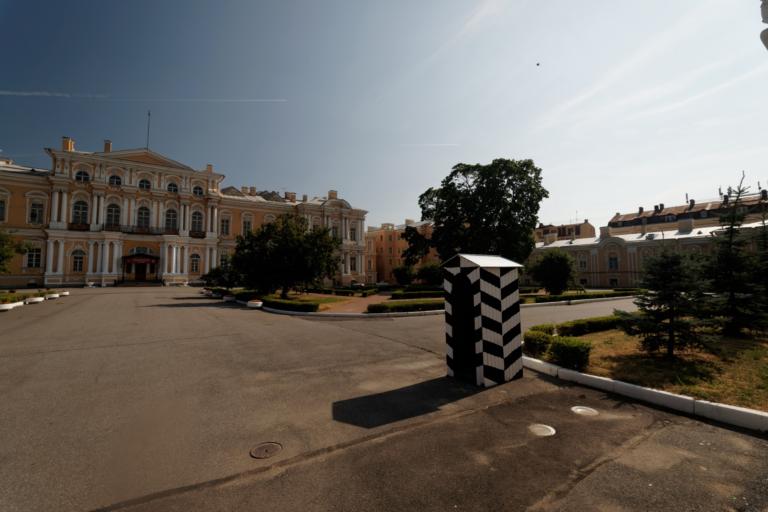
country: RU
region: St.-Petersburg
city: Saint Petersburg
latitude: 59.9320
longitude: 30.3306
